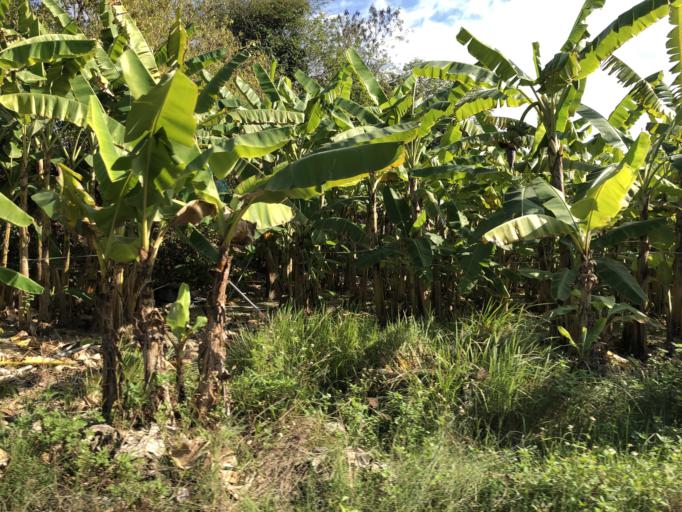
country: TW
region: Taiwan
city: Yujing
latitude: 23.0186
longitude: 120.3973
